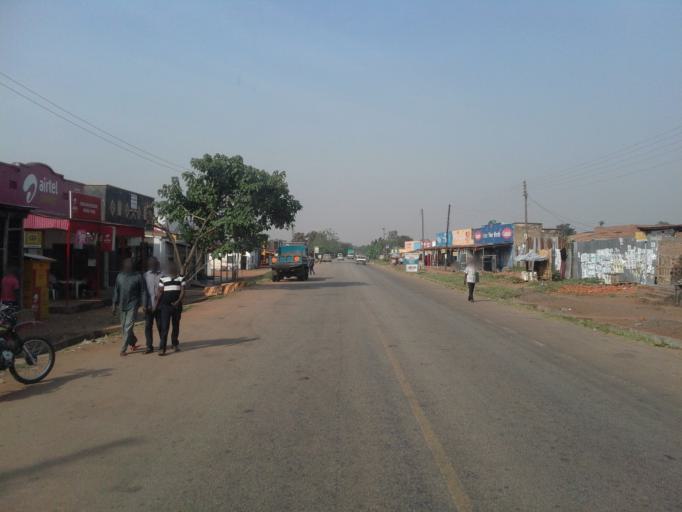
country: UG
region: Eastern Region
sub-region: Budaka District
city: Budaka
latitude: 1.0158
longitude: 33.9489
